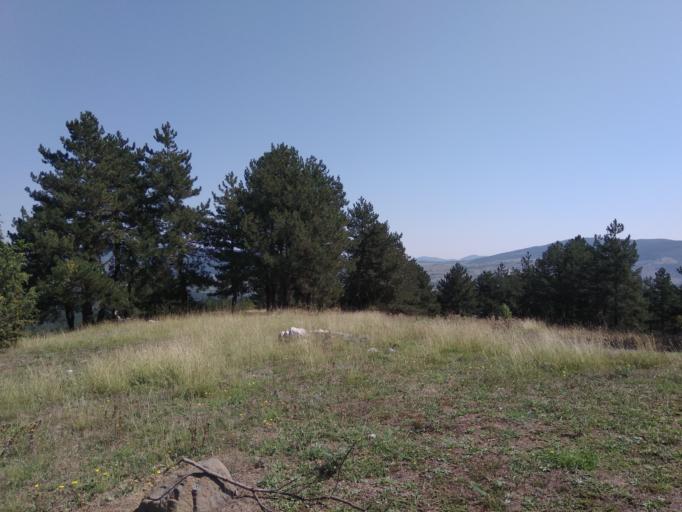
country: BG
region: Kurdzhali
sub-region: Obshtina Kurdzhali
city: Kurdzhali
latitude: 41.6338
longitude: 25.4527
